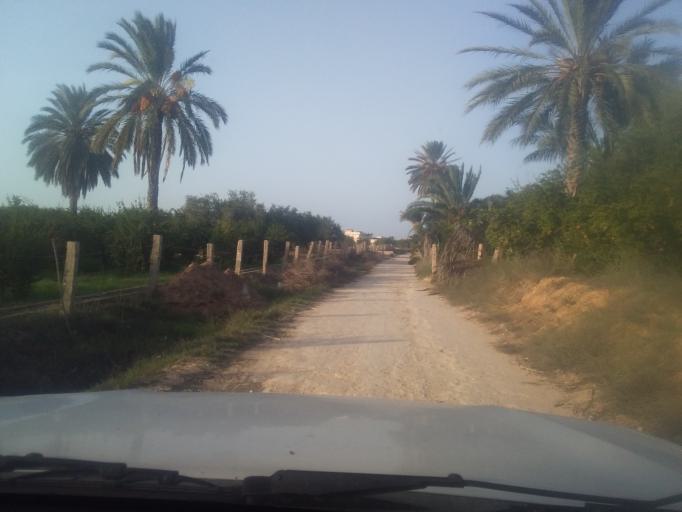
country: TN
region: Qabis
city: Gabes
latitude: 33.6308
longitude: 10.2913
